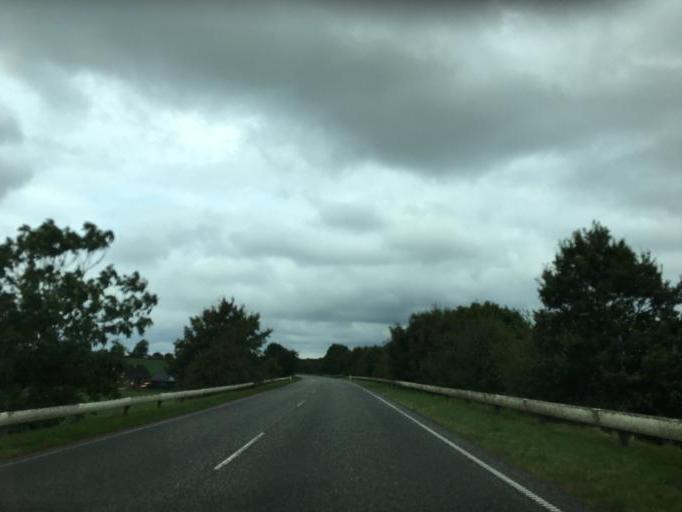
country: DK
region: South Denmark
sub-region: Kolding Kommune
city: Kolding
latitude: 55.5786
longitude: 9.4997
